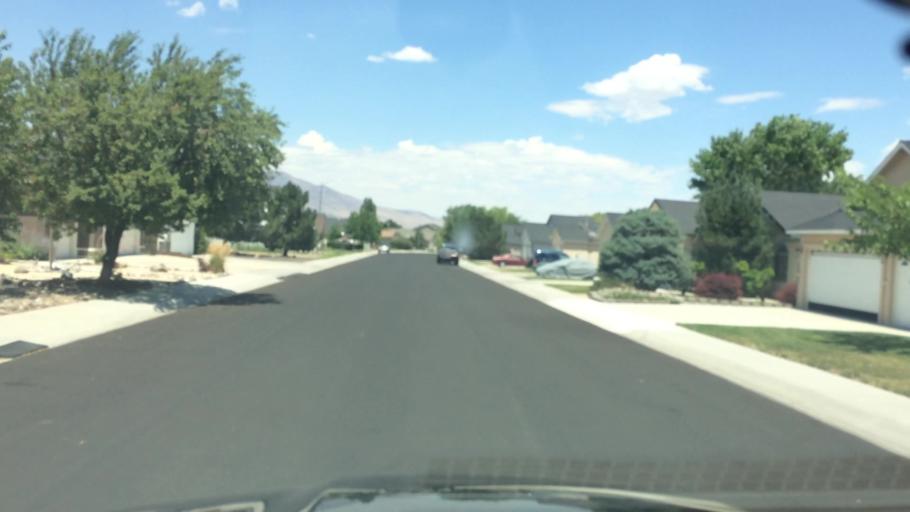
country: US
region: Nevada
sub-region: Lyon County
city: Fernley
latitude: 39.5856
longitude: -119.1411
